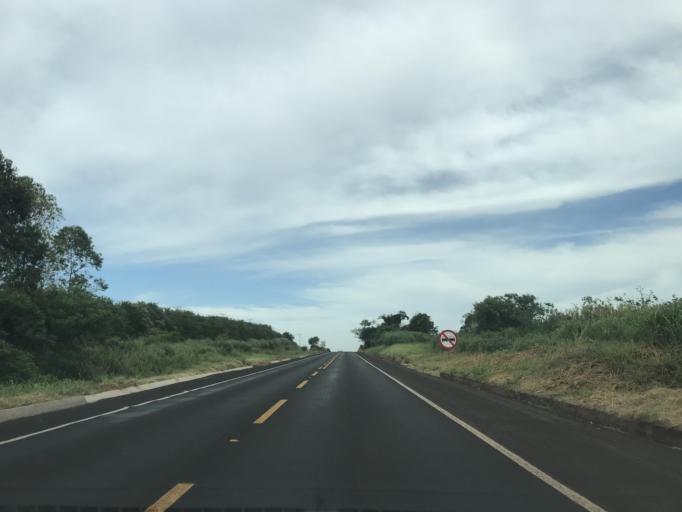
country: BR
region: Parana
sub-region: Paranavai
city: Paranavai
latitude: -23.0169
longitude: -52.5075
